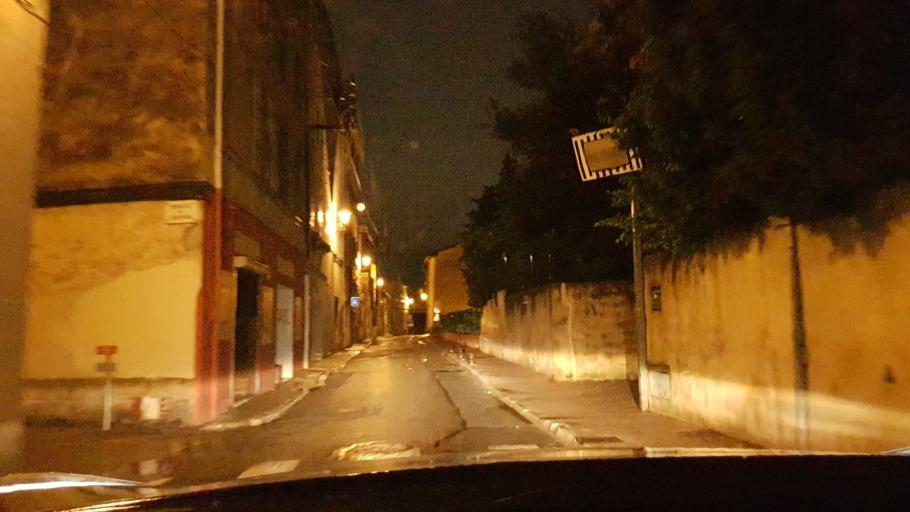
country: FR
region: Provence-Alpes-Cote d'Azur
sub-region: Departement des Alpes-Maritimes
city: Vallauris
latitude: 43.5780
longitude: 7.0510
